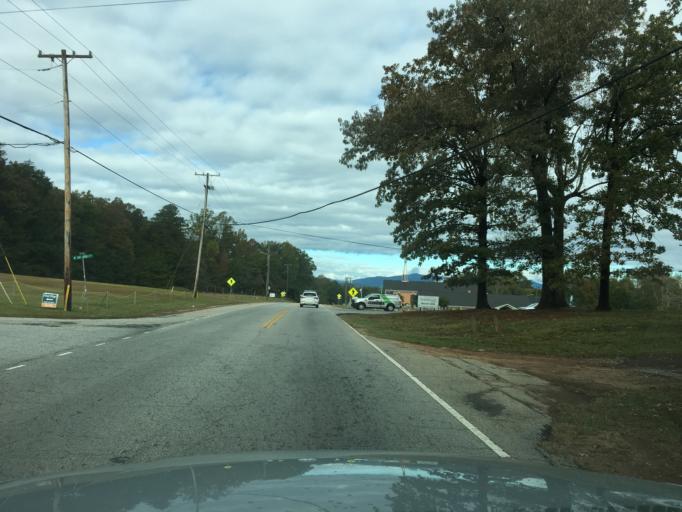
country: US
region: South Carolina
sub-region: Greenville County
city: Greer
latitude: 34.9972
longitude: -82.2490
